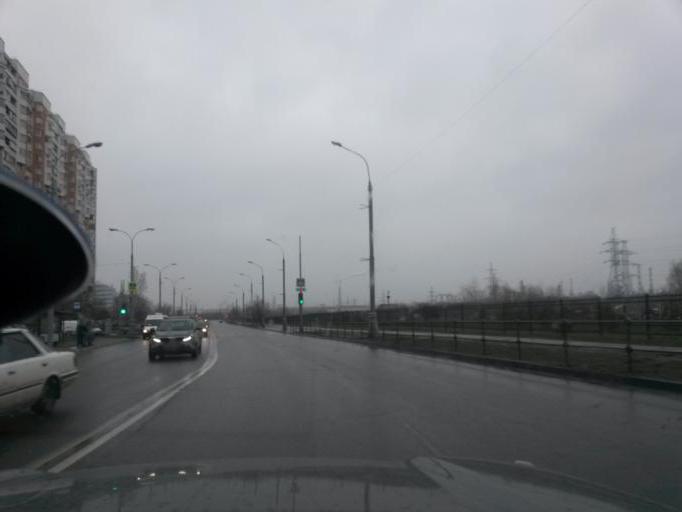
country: RU
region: Moscow
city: Brateyevo
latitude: 55.6513
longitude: 37.7720
